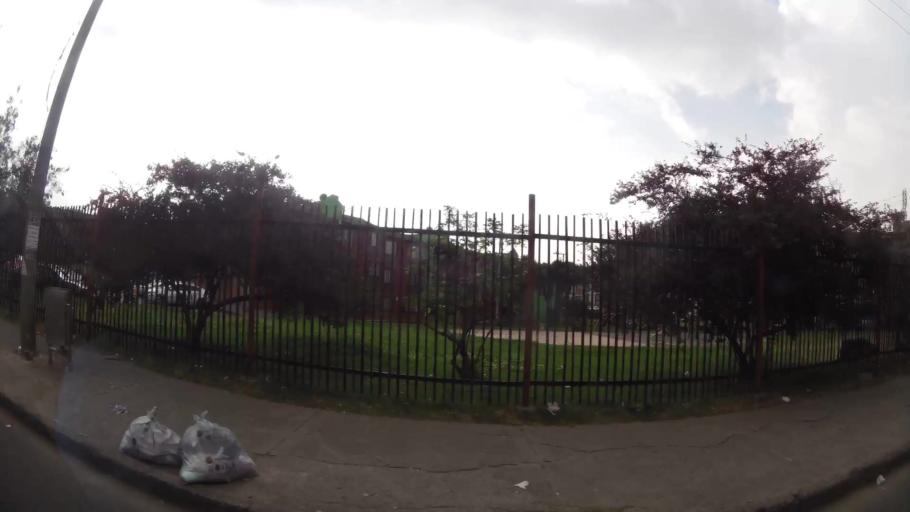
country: CO
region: Bogota D.C.
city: Bogota
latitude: 4.5548
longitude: -74.1127
